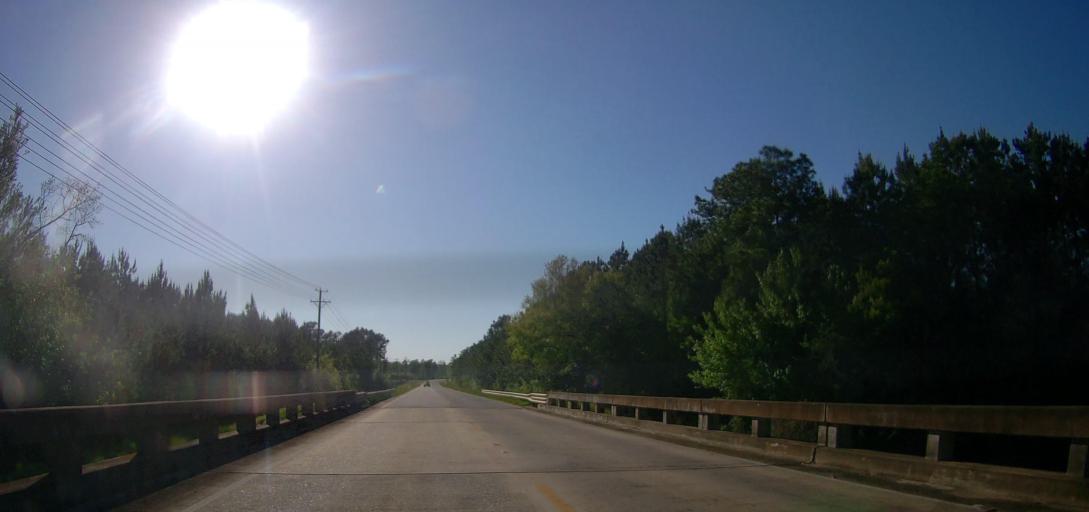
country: US
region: Georgia
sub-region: Ben Hill County
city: Fitzgerald
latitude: 31.6939
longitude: -83.2916
